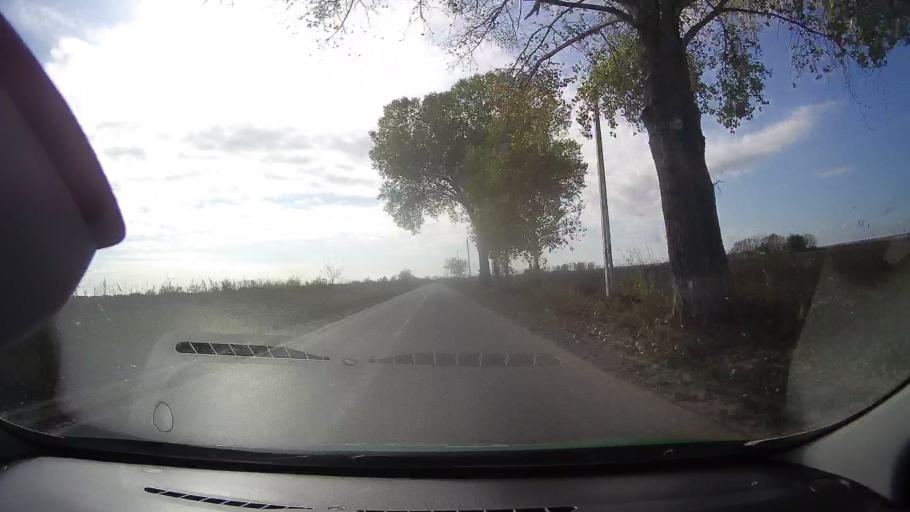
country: RO
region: Tulcea
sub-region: Comuna Sarichioi
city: Sarichioi
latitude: 44.9849
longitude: 28.8841
